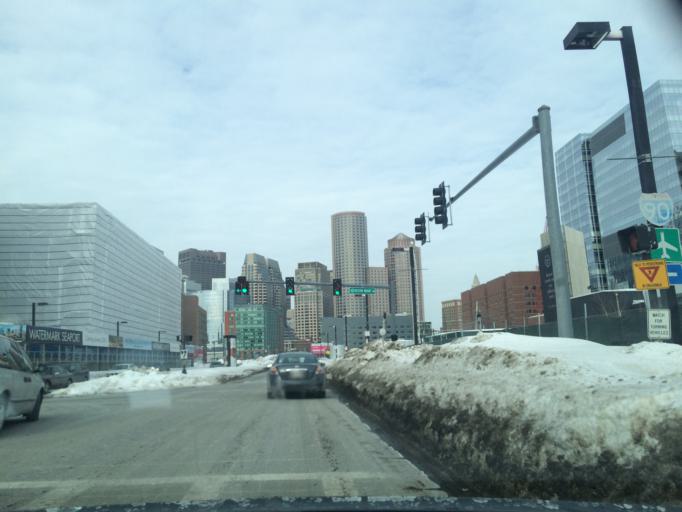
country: US
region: Massachusetts
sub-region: Suffolk County
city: Boston
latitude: 42.3516
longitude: -71.0452
